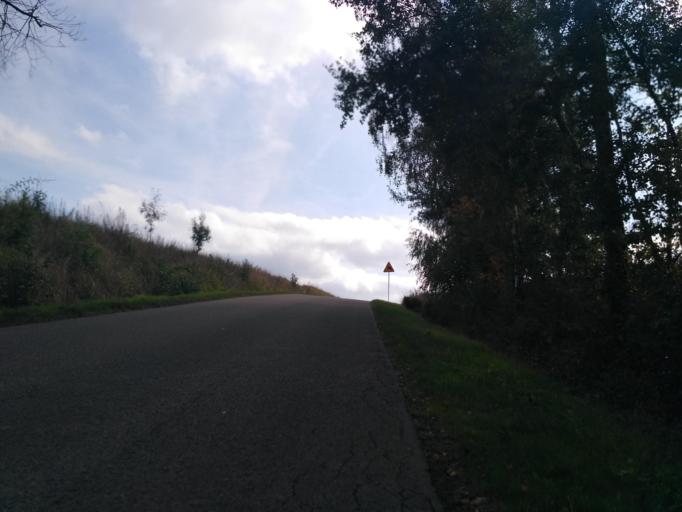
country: PL
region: Subcarpathian Voivodeship
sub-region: Powiat ropczycko-sedziszowski
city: Wielopole Skrzynskie
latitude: 49.9275
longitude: 21.5654
